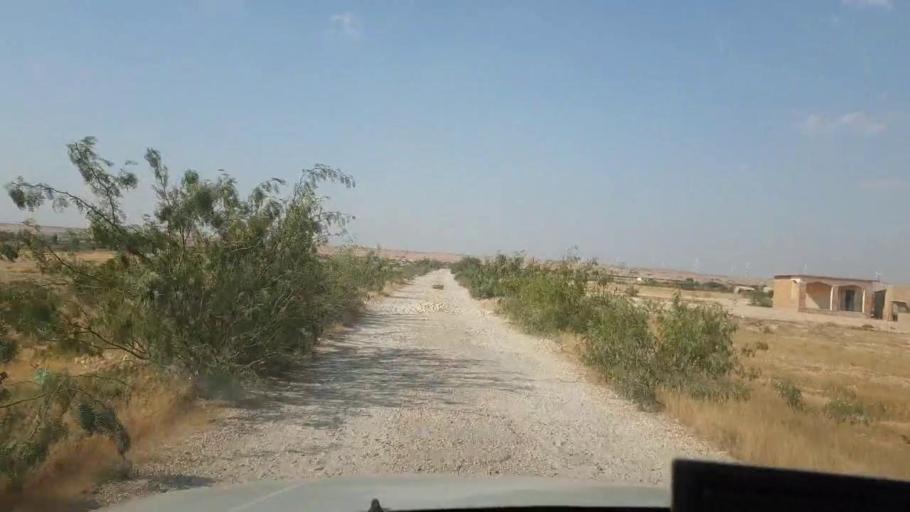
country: PK
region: Sindh
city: Daro Mehar
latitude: 25.0719
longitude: 68.0965
